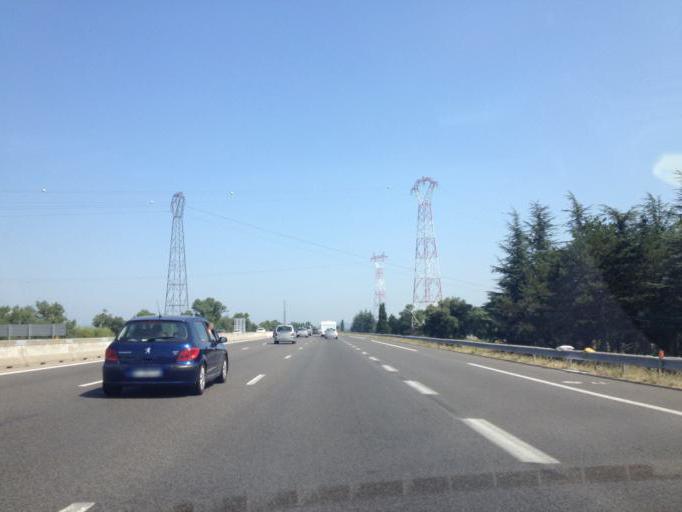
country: FR
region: Rhone-Alpes
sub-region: Departement de la Drome
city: Saint-Paul-Trois-Chateaux
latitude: 44.3284
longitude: 4.7392
